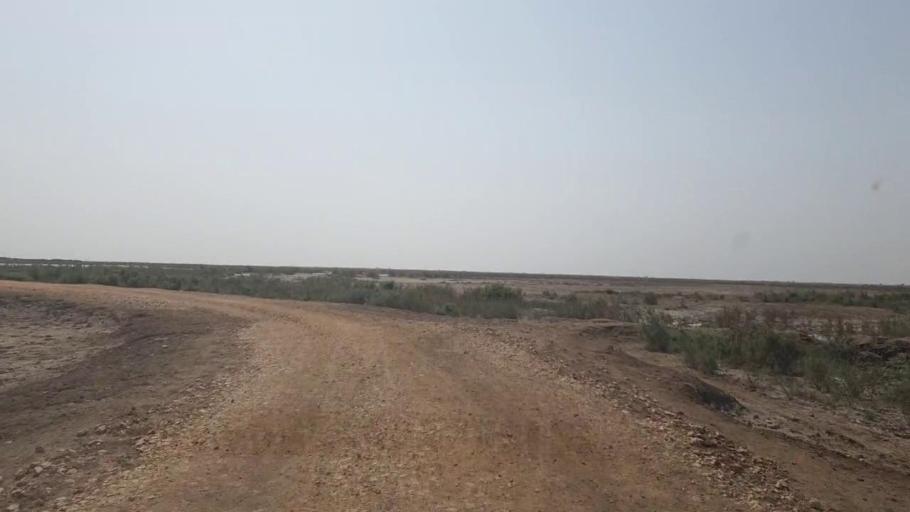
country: PK
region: Sindh
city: Jati
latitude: 24.3730
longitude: 68.6020
